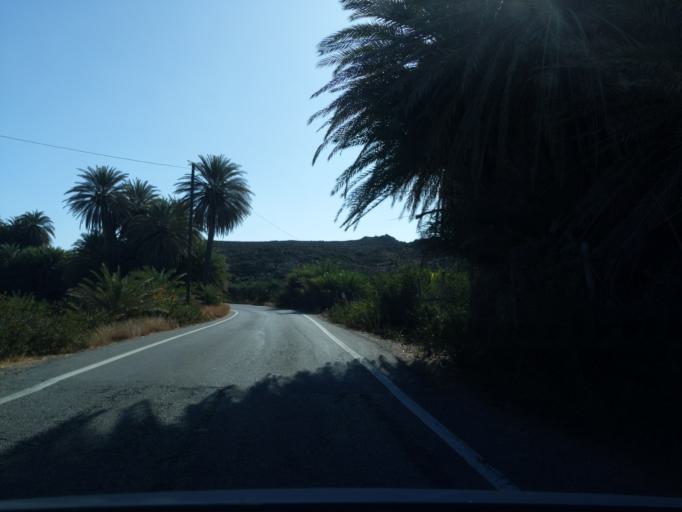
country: GR
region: Crete
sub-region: Nomos Lasithiou
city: Palekastro
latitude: 35.2537
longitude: 26.2542
